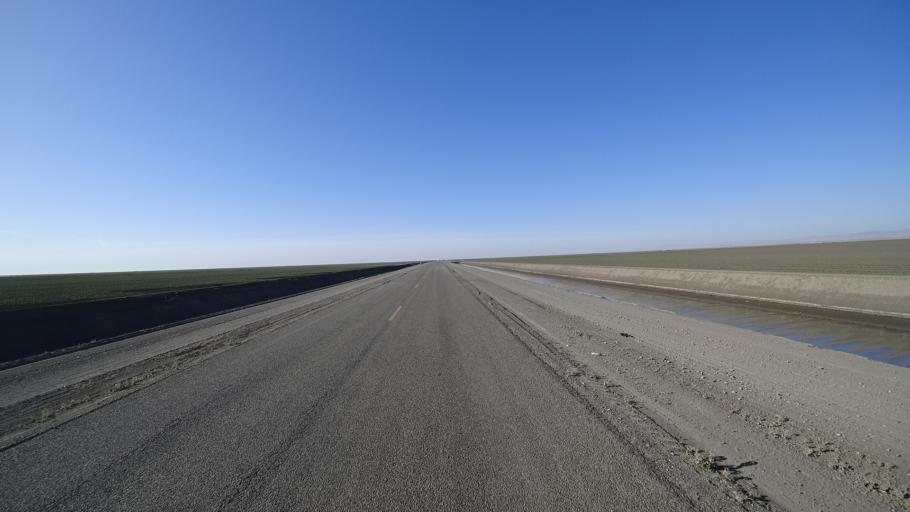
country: US
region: California
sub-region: Kings County
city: Stratford
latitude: 36.1332
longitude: -119.7981
